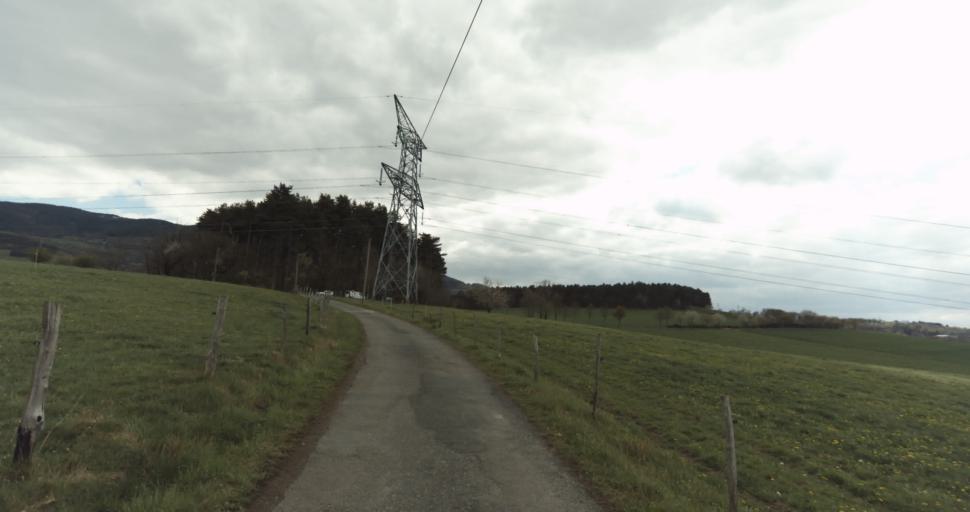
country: FR
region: Rhone-Alpes
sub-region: Departement de la Loire
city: Saint-Jean-Bonnefonds
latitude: 45.4509
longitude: 4.4643
